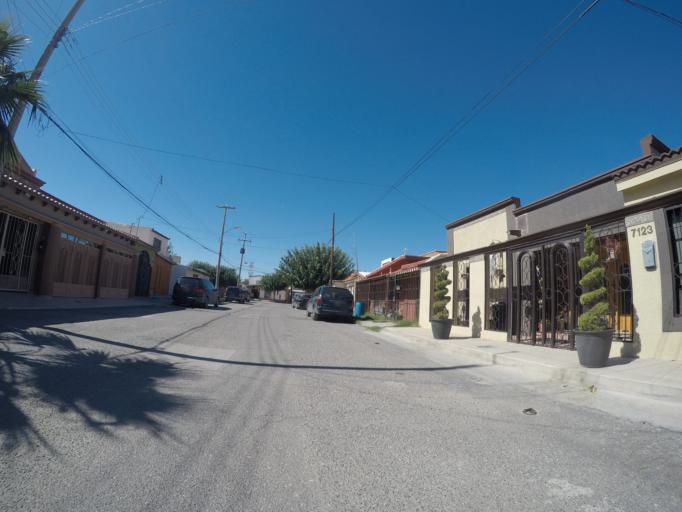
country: MX
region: Chihuahua
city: Ciudad Juarez
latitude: 31.7221
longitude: -106.4204
